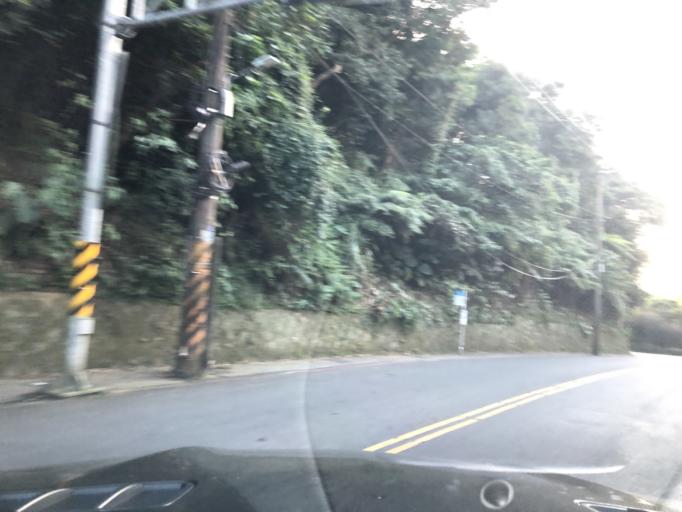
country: TW
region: Taipei
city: Taipei
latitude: 25.1423
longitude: 121.5564
